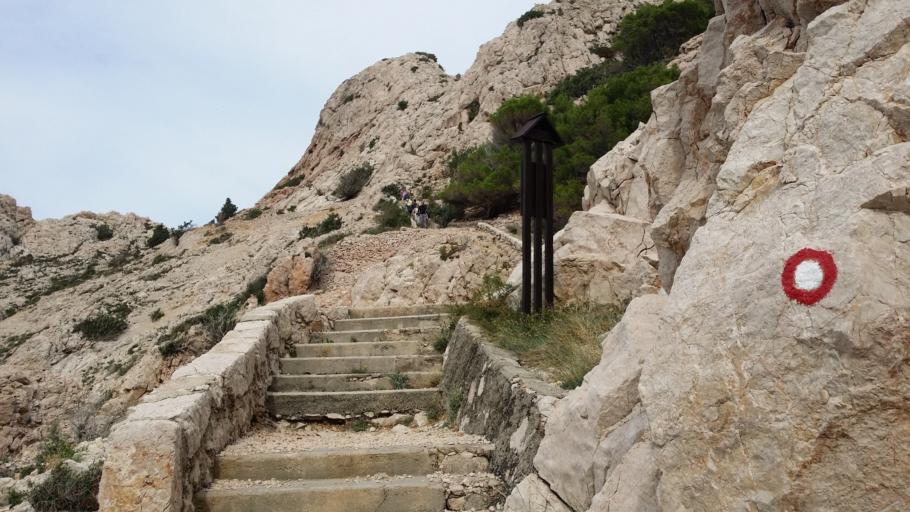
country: HR
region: Primorsko-Goranska
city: Banjol
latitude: 44.7005
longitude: 14.8976
